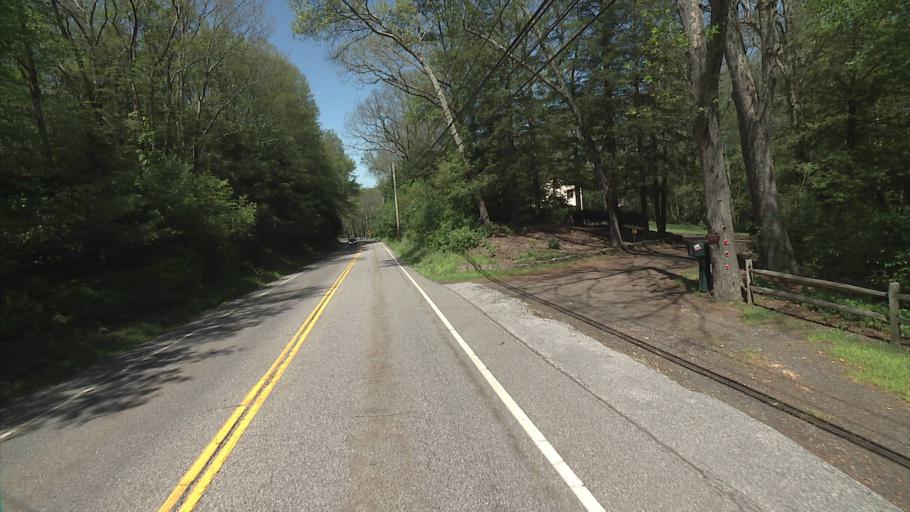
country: US
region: Connecticut
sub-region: Middlesex County
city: Moodus
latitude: 41.5494
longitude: -72.4357
